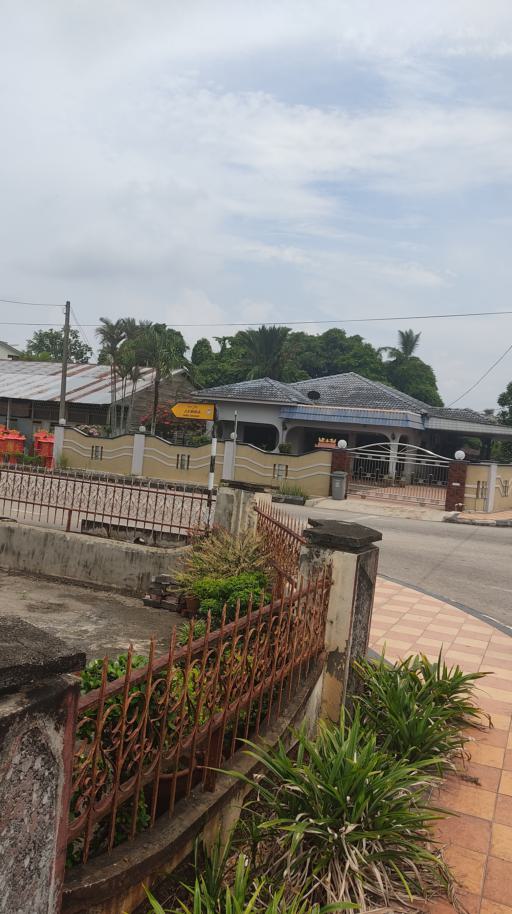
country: MY
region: Johor
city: Tangkak
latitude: 2.2721
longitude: 102.5445
